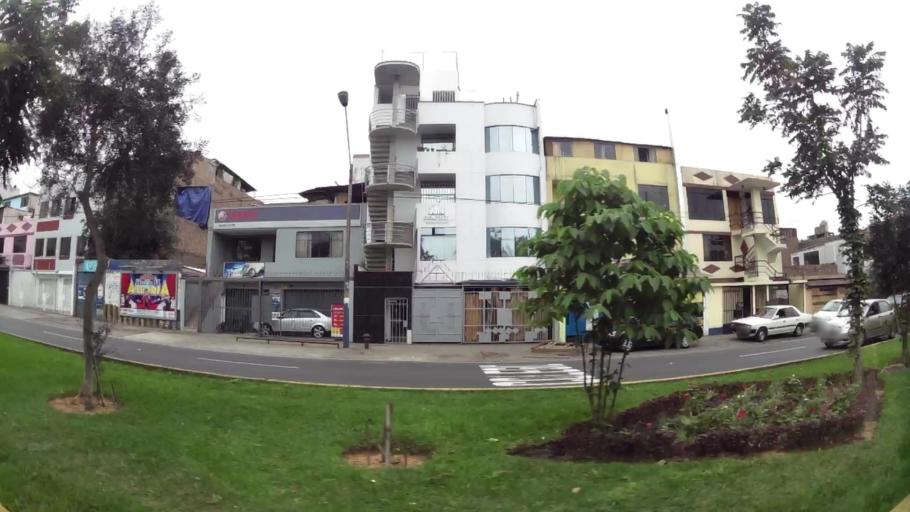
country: PE
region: Lima
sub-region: Lima
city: San Luis
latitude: -12.0781
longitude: -76.9987
